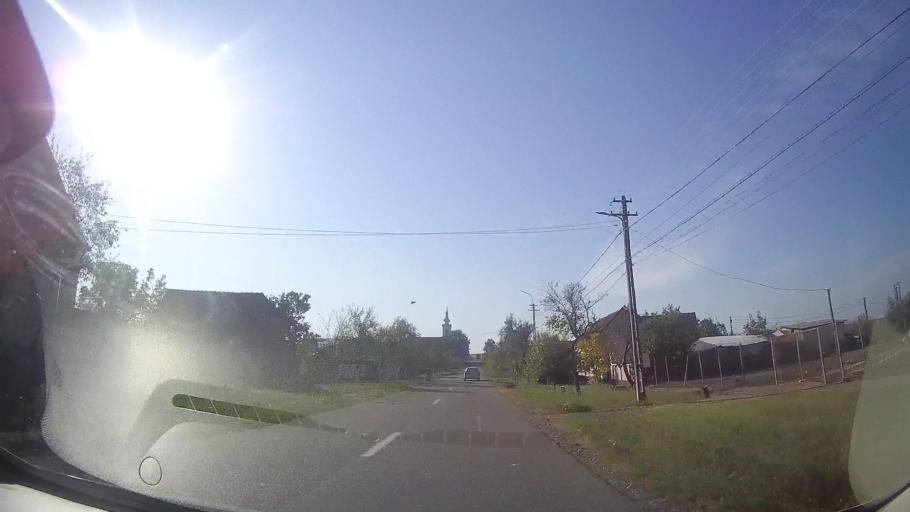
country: RO
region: Timis
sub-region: Oras Recas
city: Recas
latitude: 45.8605
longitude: 21.5152
